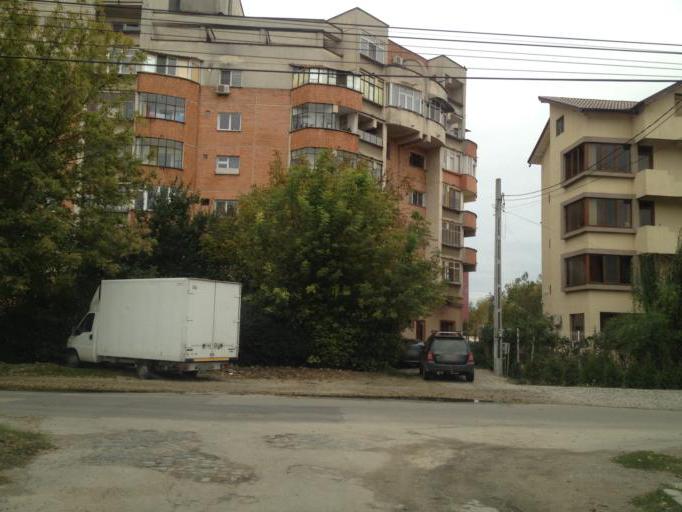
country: RO
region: Dolj
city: Craiova
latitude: 44.3331
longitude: 23.7739
